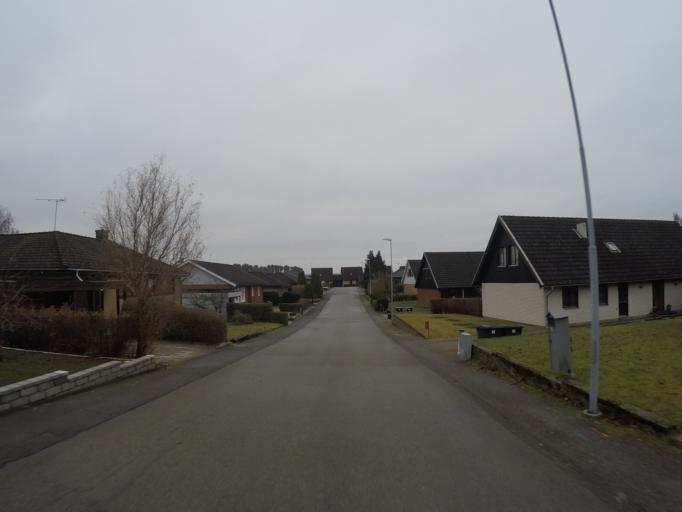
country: SE
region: Skane
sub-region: Eslovs Kommun
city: Eslov
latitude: 55.7534
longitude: 13.3718
